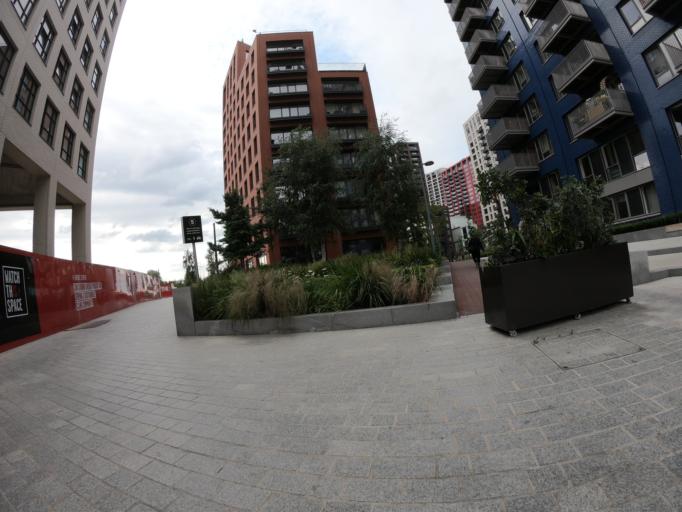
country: GB
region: England
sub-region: Greater London
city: Poplar
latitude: 51.5109
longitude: 0.0054
